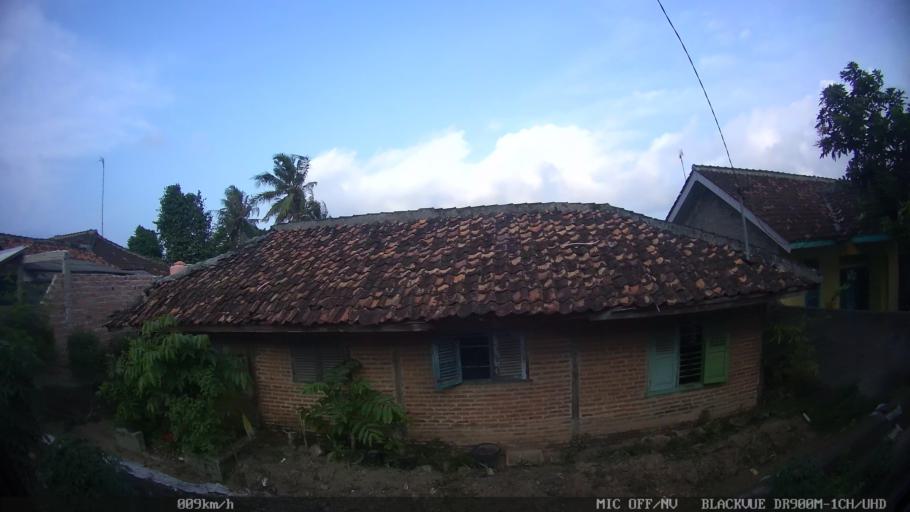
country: ID
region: Lampung
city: Kedaton
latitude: -5.4018
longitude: 105.2945
